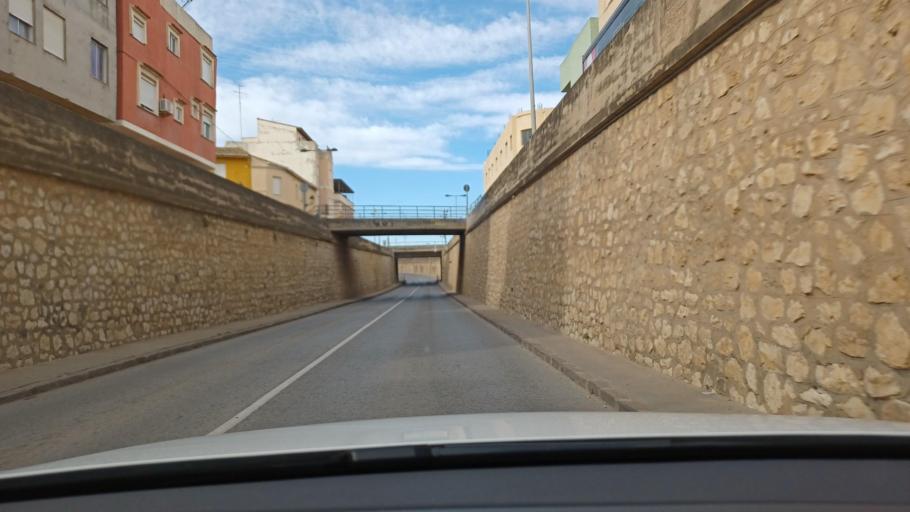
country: ES
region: Valencia
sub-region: Provincia de Valencia
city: Benifaio
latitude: 39.2888
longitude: -0.4285
